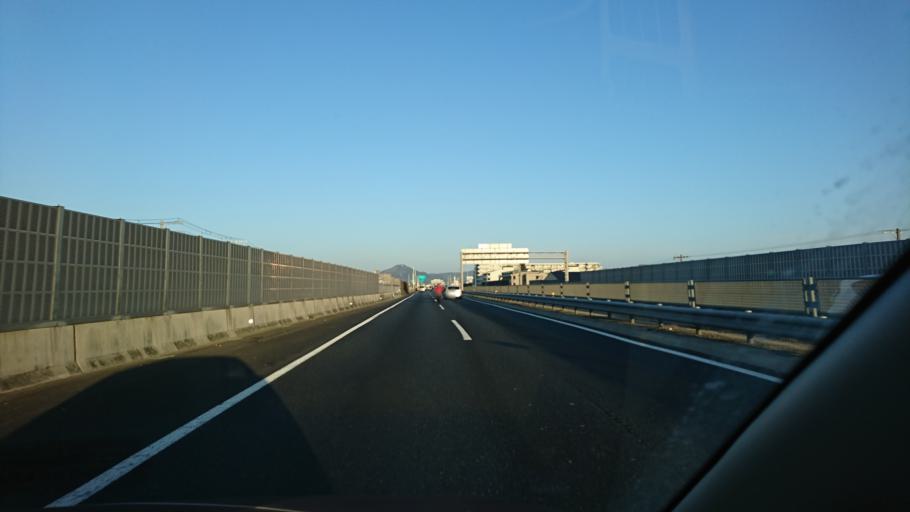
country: JP
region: Hyogo
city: Kakogawacho-honmachi
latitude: 34.7672
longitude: 134.8486
